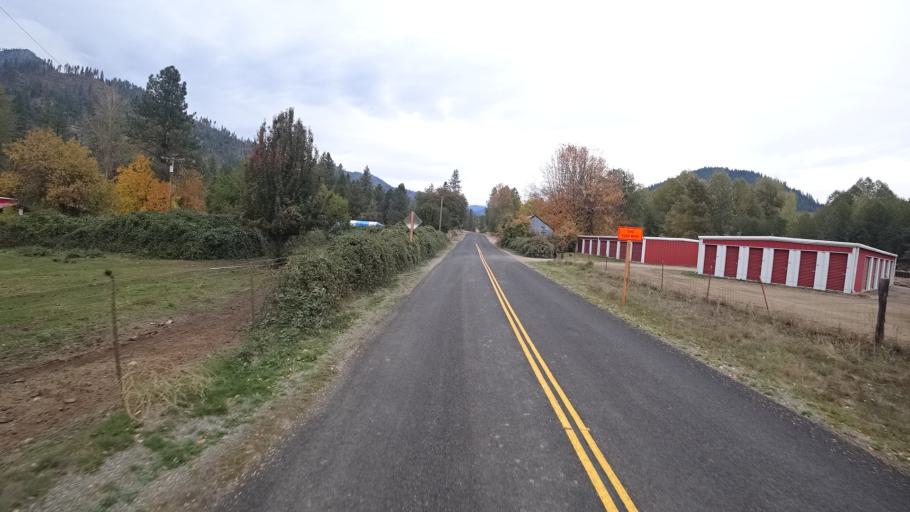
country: US
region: California
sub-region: Siskiyou County
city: Happy Camp
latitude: 41.8431
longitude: -123.1978
